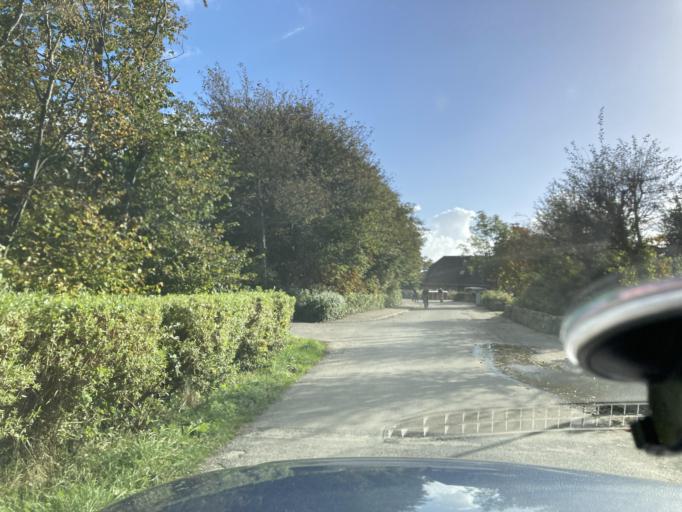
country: DE
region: Schleswig-Holstein
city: Busumer Deichhausen
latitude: 54.1396
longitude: 8.8903
